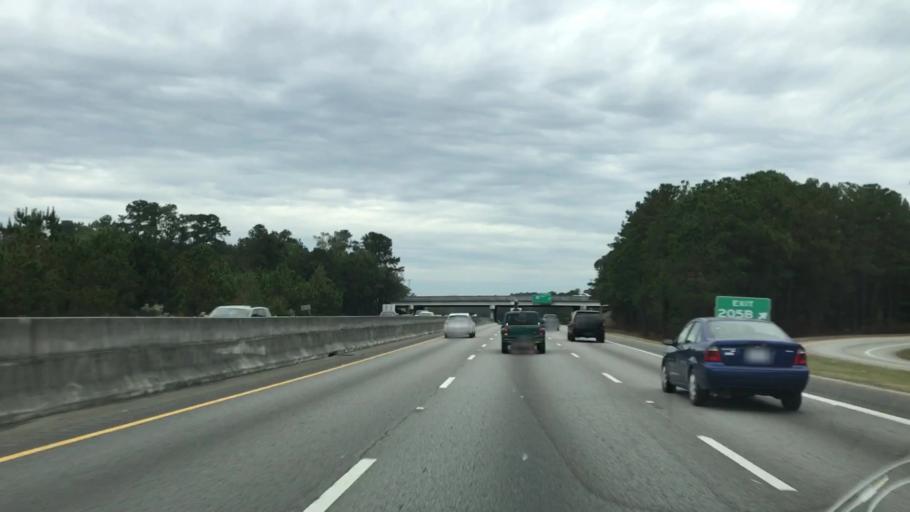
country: US
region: South Carolina
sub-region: Berkeley County
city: Ladson
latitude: 32.9766
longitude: -80.0766
